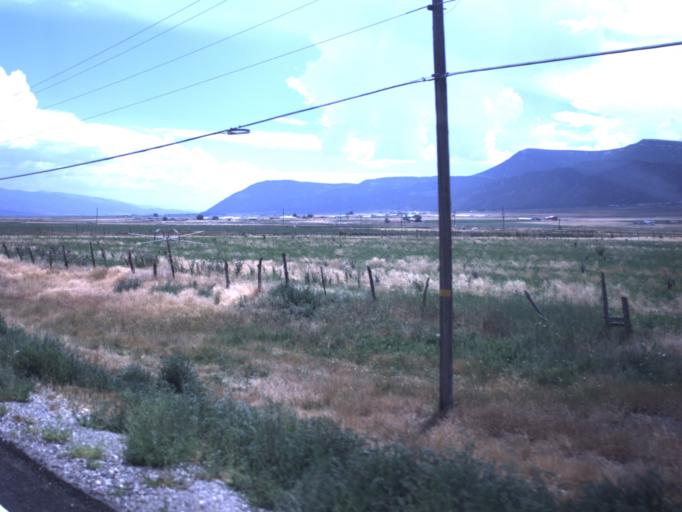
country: US
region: Utah
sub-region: Sanpete County
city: Fountain Green
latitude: 39.5918
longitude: -111.6175
